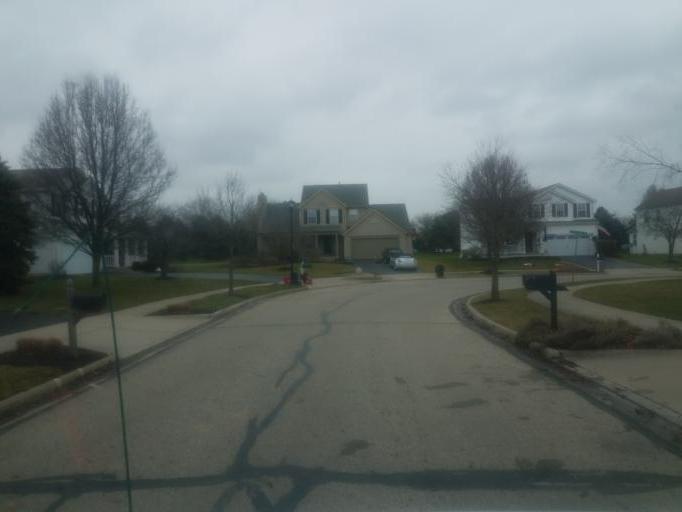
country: US
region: Ohio
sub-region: Franklin County
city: Westerville
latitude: 40.1372
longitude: -82.9618
